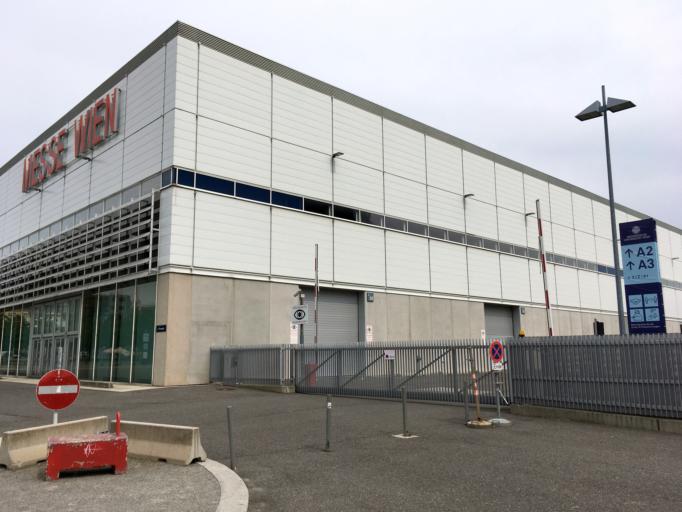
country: AT
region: Vienna
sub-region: Wien Stadt
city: Vienna
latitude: 48.2162
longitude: 16.4059
